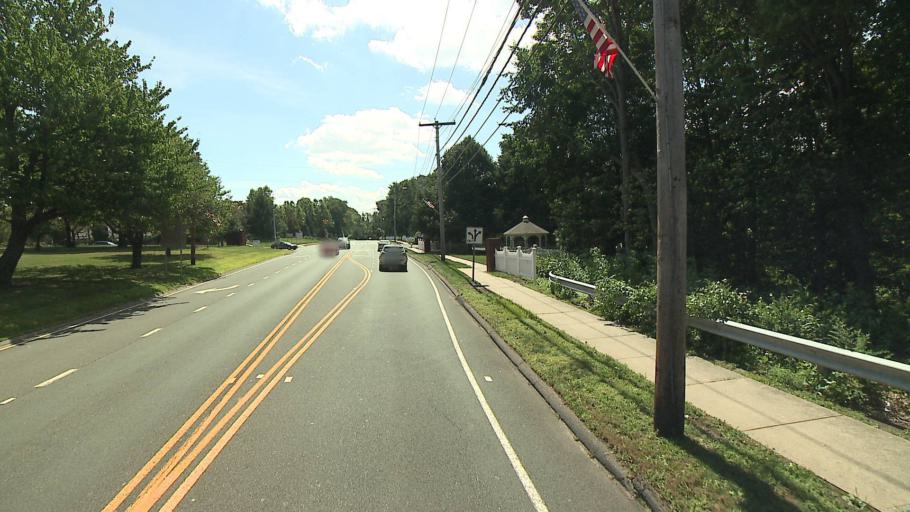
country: US
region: Connecticut
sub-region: Fairfield County
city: Trumbull
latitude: 41.2569
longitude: -73.2195
